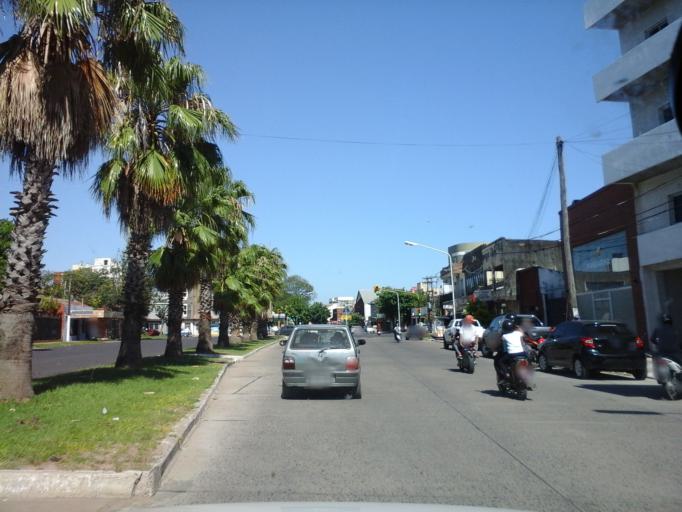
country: AR
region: Corrientes
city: Corrientes
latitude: -27.4669
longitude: -58.8170
